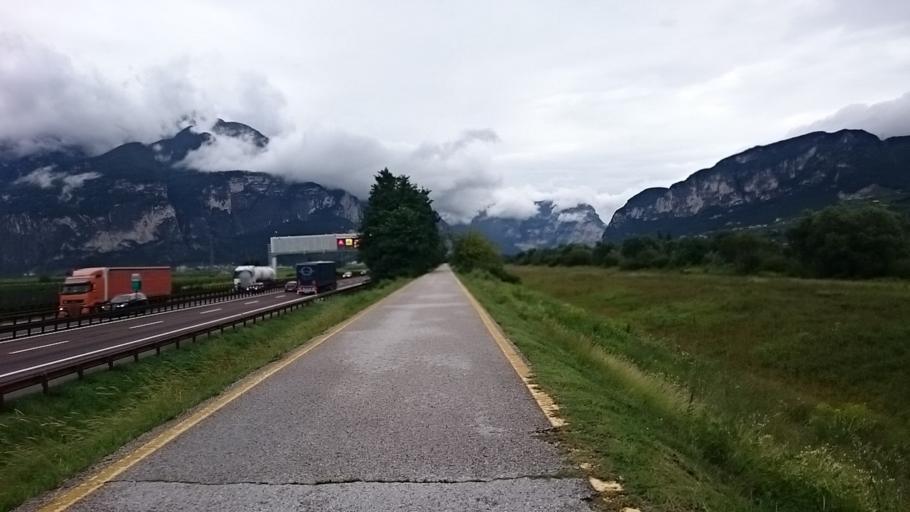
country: IT
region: Trentino-Alto Adige
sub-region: Provincia di Trento
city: Nave San Rocco
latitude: 46.1812
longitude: 11.1130
